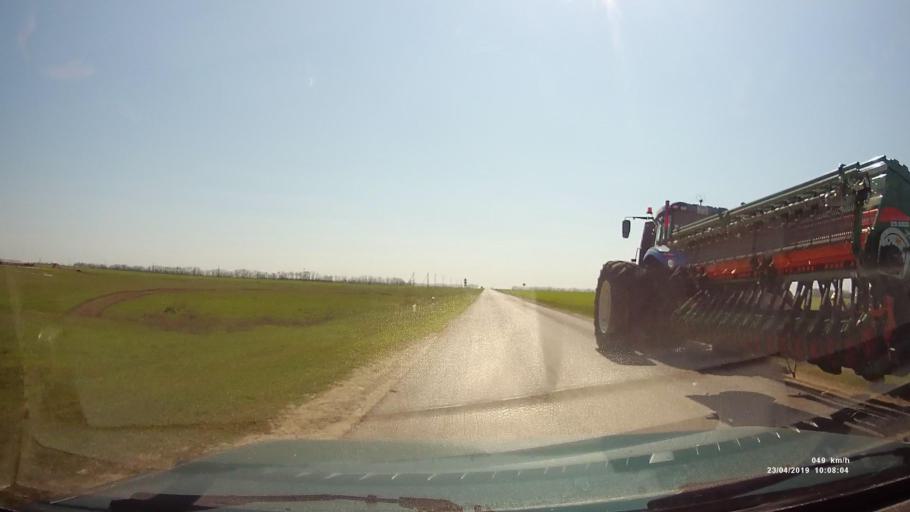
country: RU
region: Rostov
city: Sovetskoye
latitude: 46.7215
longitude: 42.2611
